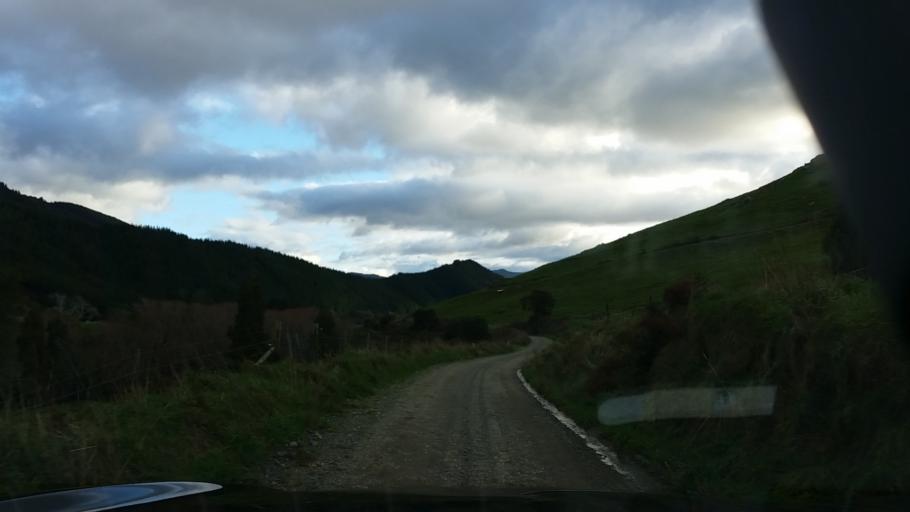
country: NZ
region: Nelson
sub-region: Nelson City
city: Nelson
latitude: -41.2086
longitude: 173.6351
